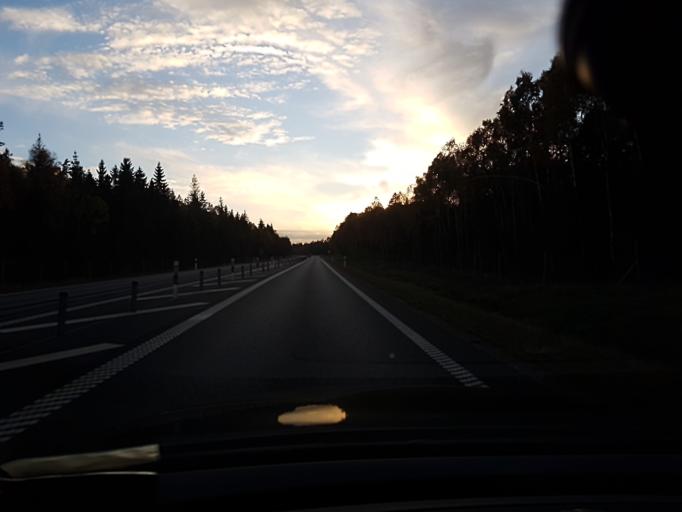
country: SE
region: Kronoberg
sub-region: Ljungby Kommun
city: Ljungby
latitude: 56.7902
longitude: 13.8403
